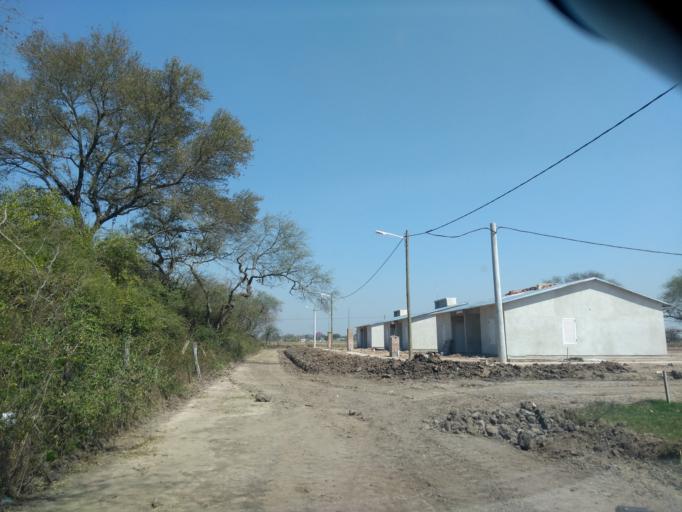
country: AR
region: Chaco
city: Resistencia
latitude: -27.4133
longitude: -58.9558
